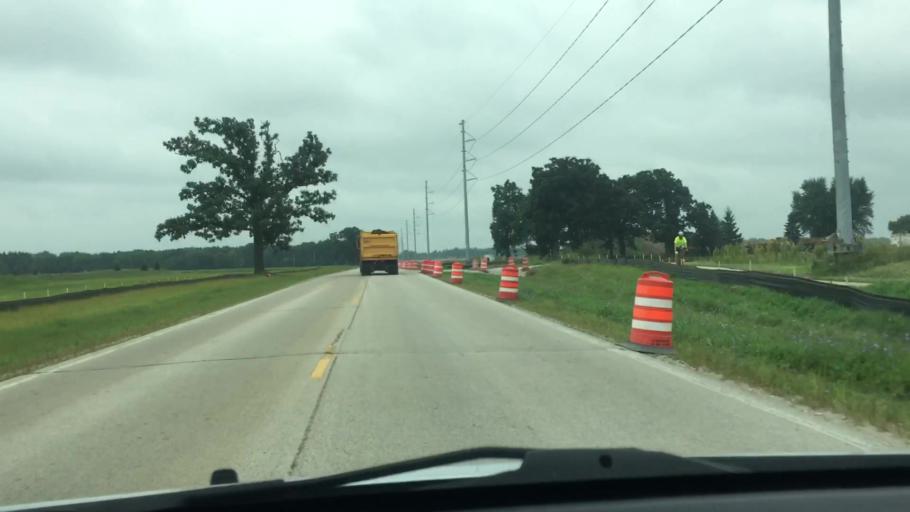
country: US
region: Wisconsin
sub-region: Waukesha County
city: Delafield
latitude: 43.0758
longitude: -88.4419
